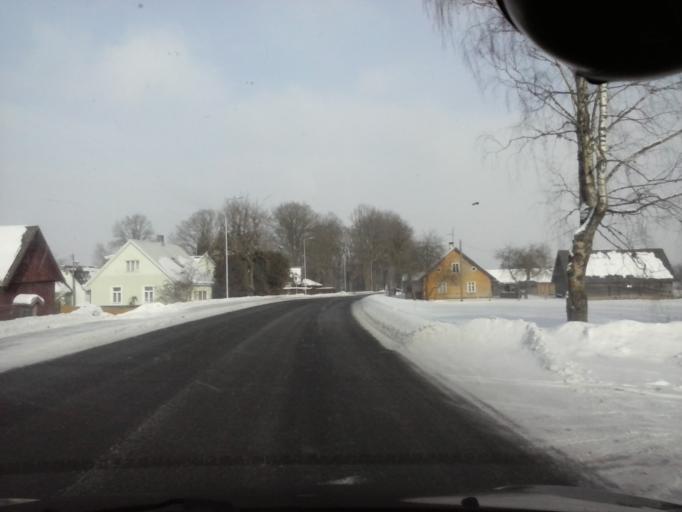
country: EE
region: Viljandimaa
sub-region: Abja vald
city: Abja-Paluoja
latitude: 58.3271
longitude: 25.3075
